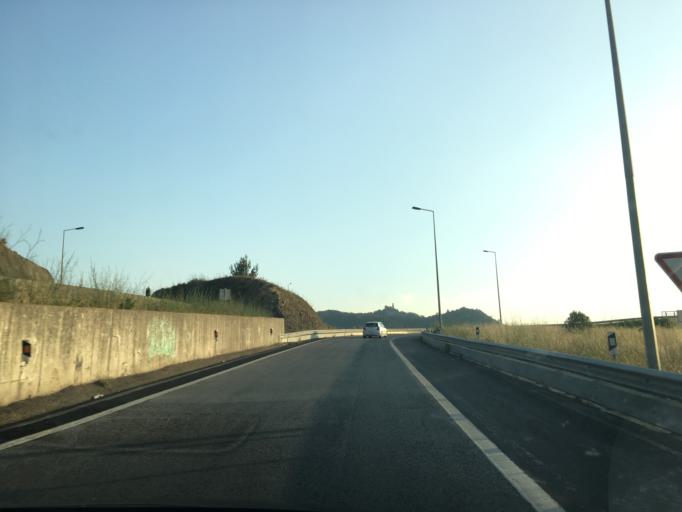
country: PT
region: Lisbon
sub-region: Sintra
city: Sintra
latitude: 38.8038
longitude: -9.3610
